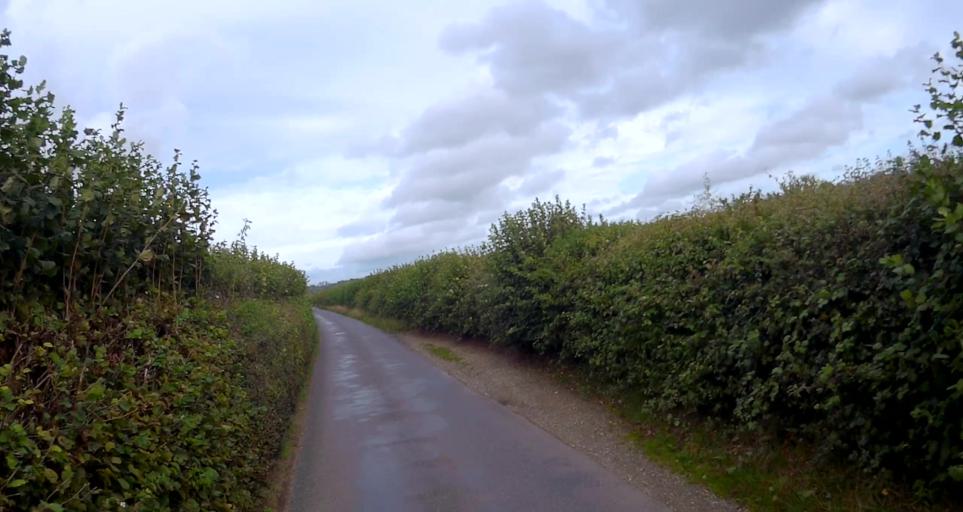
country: GB
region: England
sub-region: Hampshire
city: Four Marks
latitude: 51.1157
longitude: -1.0994
